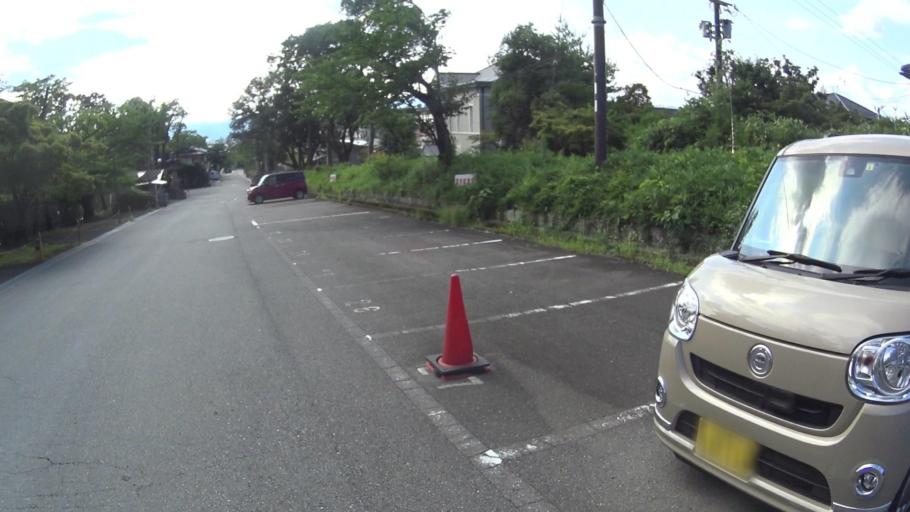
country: RU
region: Rostov
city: Remontnoye
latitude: 46.5013
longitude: 43.7592
